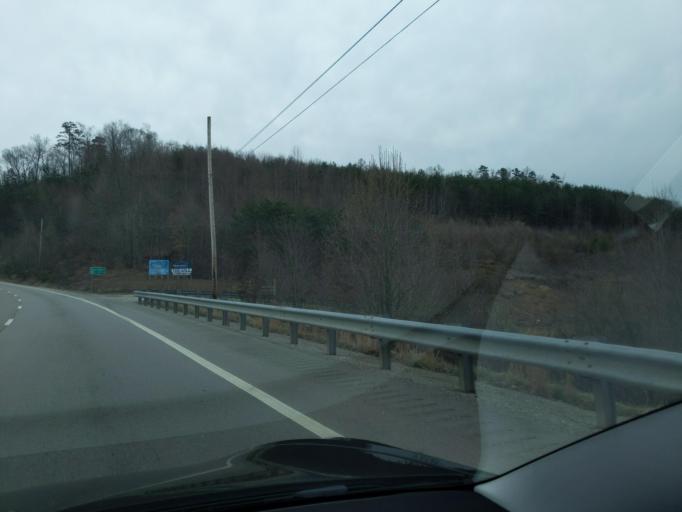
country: US
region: Kentucky
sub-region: Whitley County
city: Corbin
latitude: 36.9193
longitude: -84.1145
